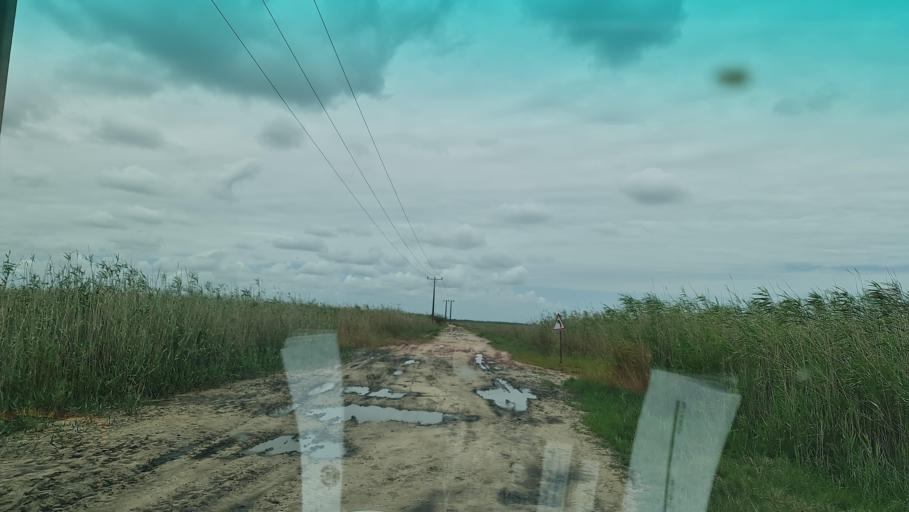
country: MZ
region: Maputo City
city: Maputo
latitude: -25.7173
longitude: 32.7012
